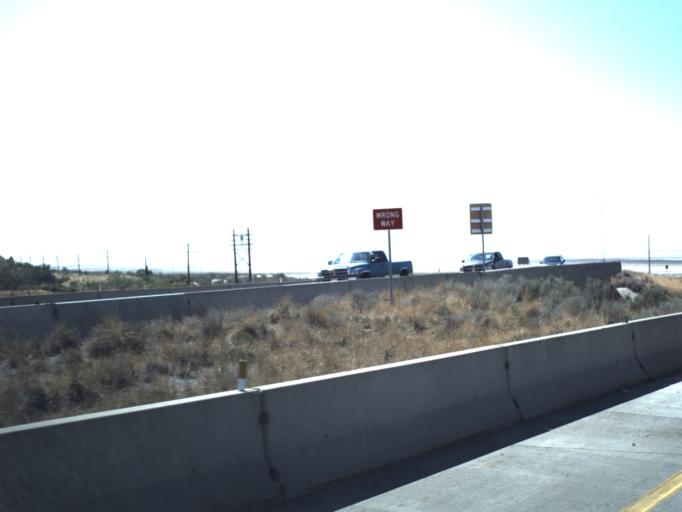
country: US
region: Utah
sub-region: Tooele County
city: Stansbury park
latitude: 40.7225
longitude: -112.2241
